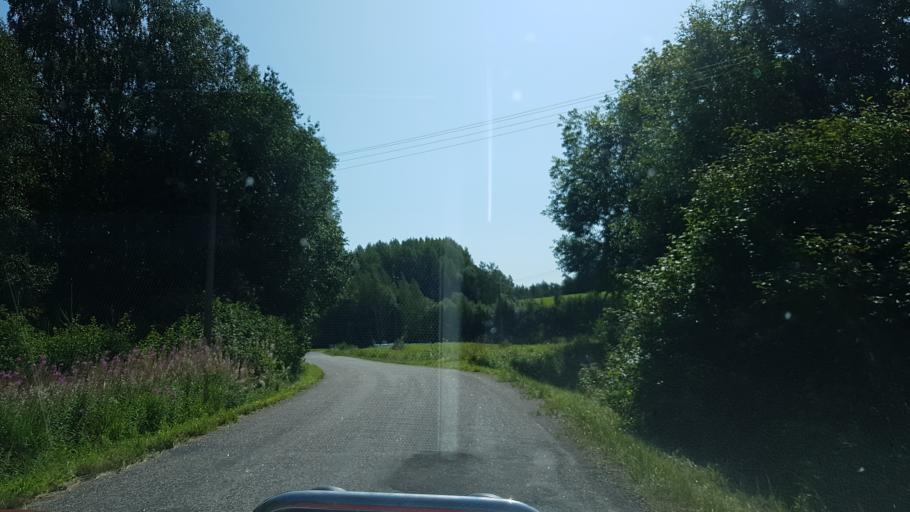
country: EE
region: Vorumaa
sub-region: Voru linn
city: Voru
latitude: 57.7104
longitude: 27.1421
